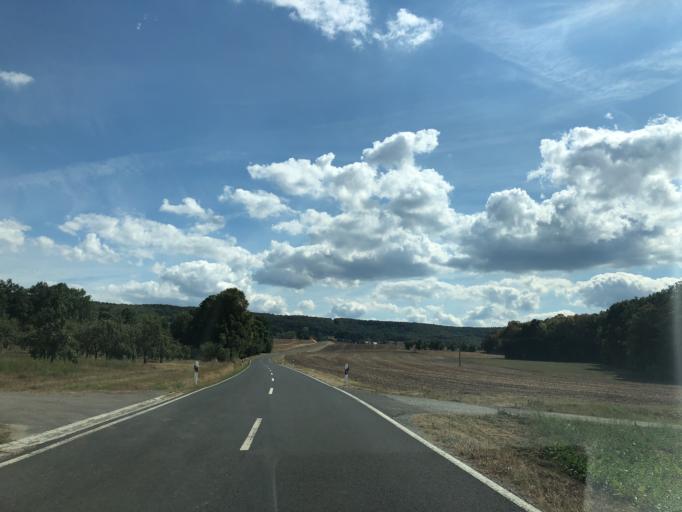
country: DE
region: Bavaria
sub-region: Regierungsbezirk Unterfranken
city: Oberschwarzach
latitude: 49.8410
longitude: 10.4318
